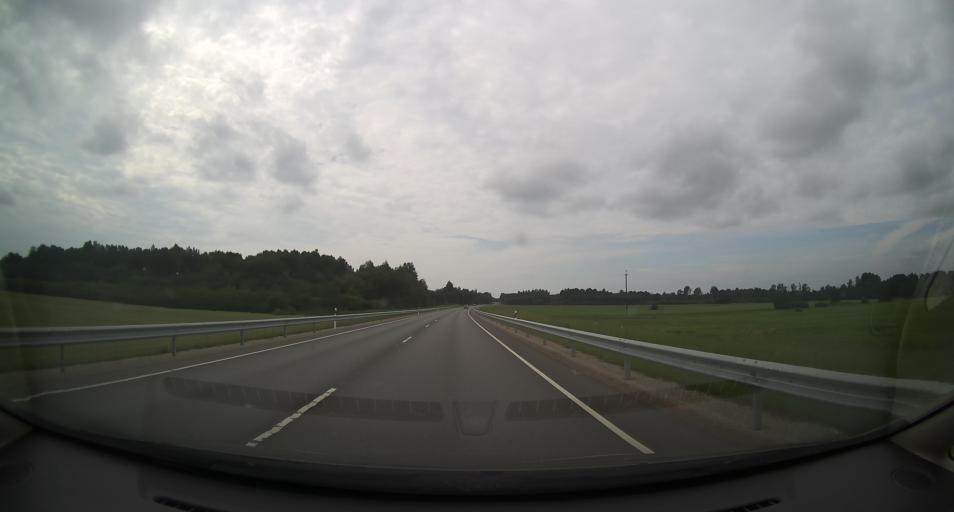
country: EE
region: Laeaene
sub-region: Lihula vald
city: Lihula
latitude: 58.6520
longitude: 23.7119
